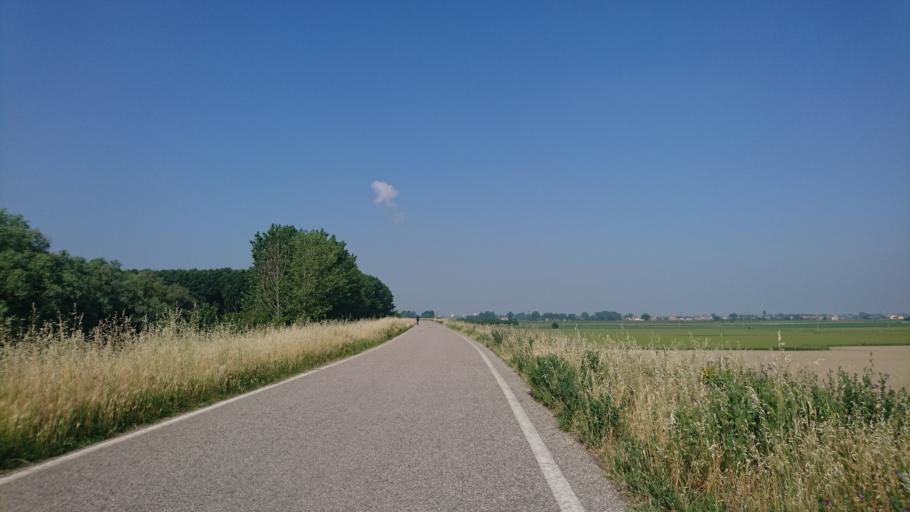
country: IT
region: Veneto
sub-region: Provincia di Rovigo
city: Melara
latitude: 45.0617
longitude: 11.1916
